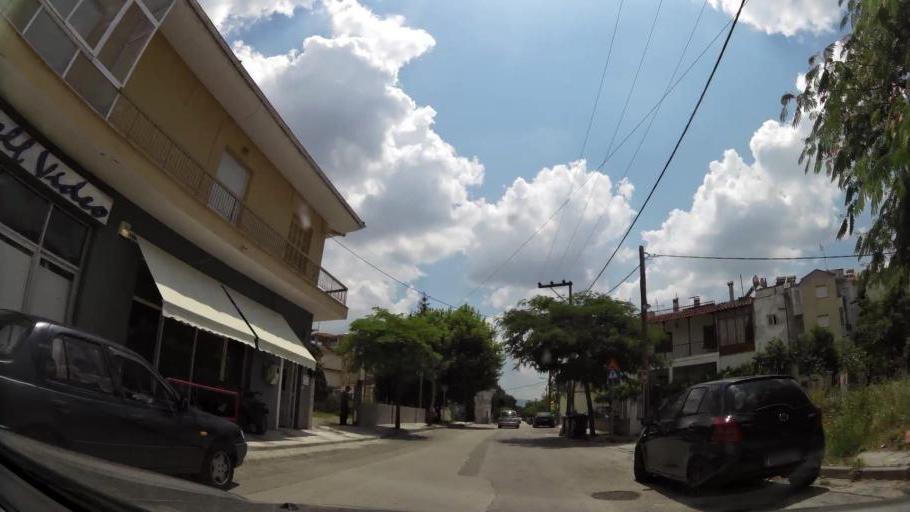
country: GR
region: West Macedonia
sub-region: Nomos Kozanis
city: Kozani
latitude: 40.2919
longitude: 21.7846
